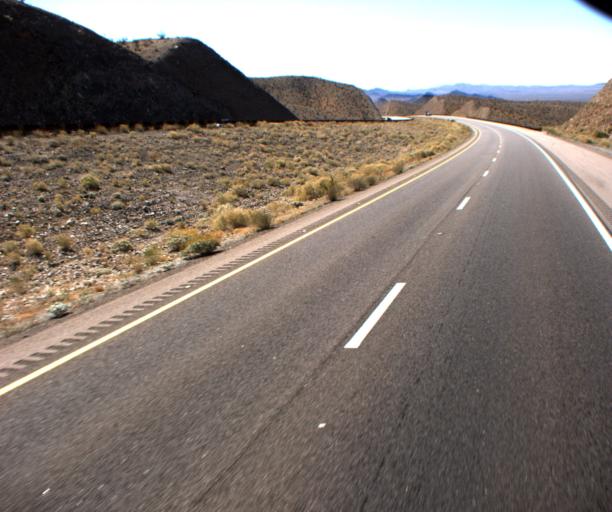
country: US
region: Nevada
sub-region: Clark County
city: Boulder City
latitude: 35.8974
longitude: -114.6263
